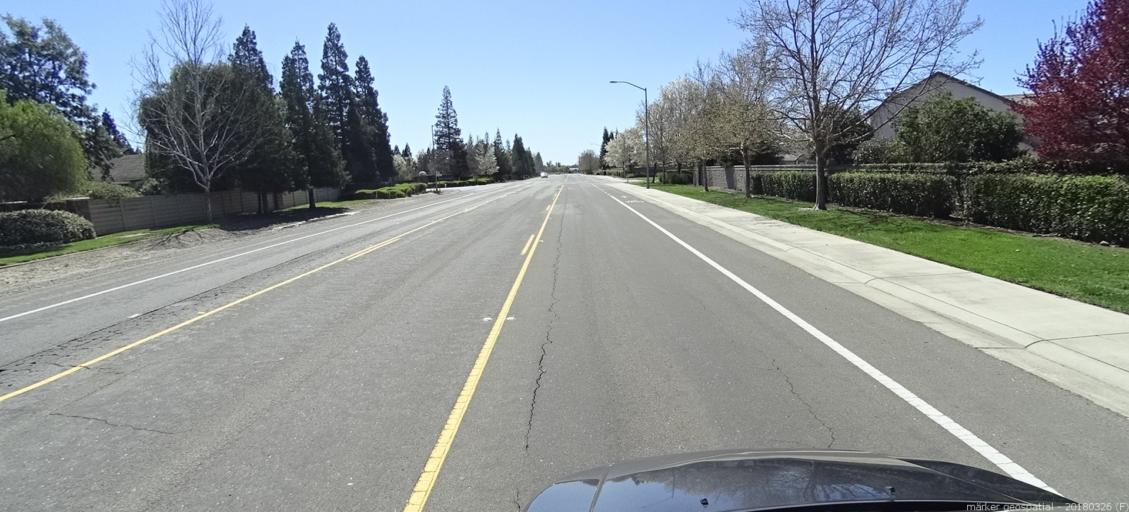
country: US
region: California
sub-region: Sacramento County
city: Vineyard
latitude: 38.4571
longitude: -121.3161
